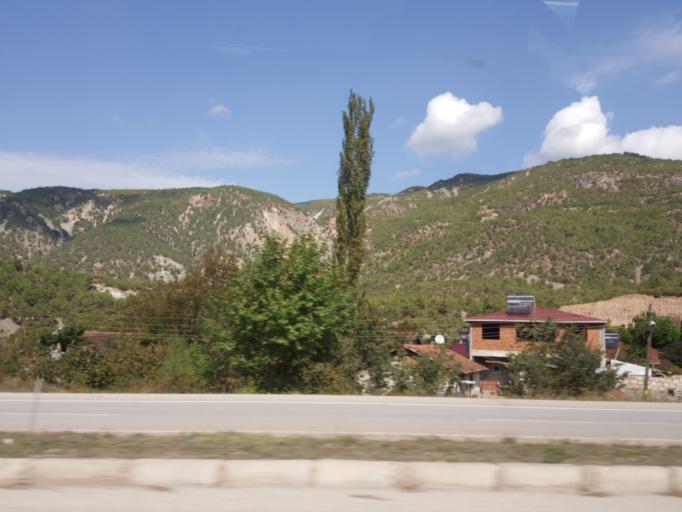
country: TR
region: Tokat
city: Basciftlik
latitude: 40.4171
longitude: 37.1933
